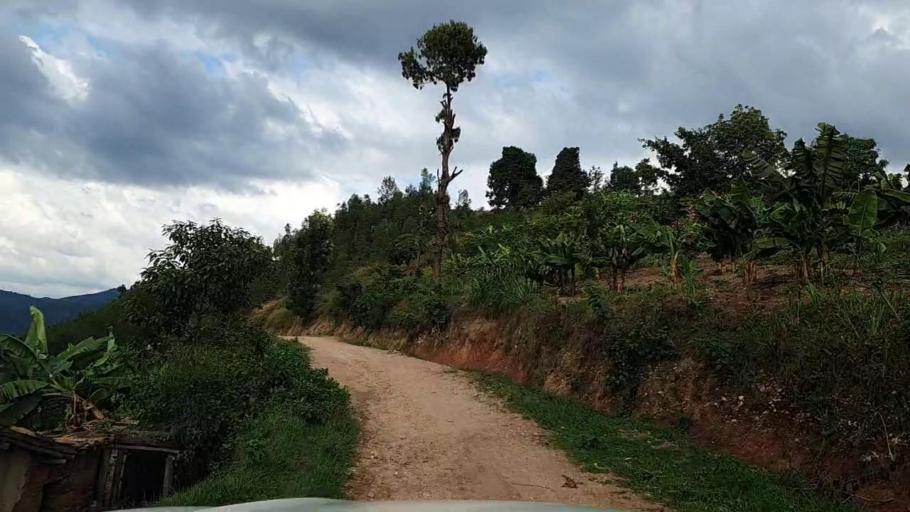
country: RW
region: Southern Province
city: Gikongoro
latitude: -2.4311
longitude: 29.6392
